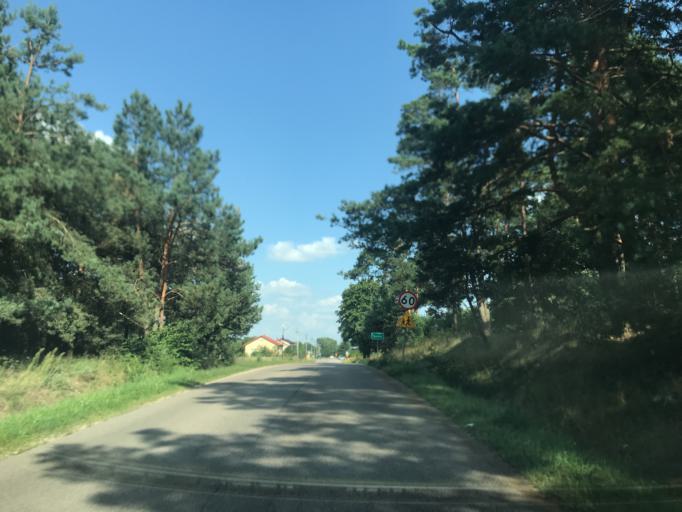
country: PL
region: Masovian Voivodeship
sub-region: Powiat mlawski
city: Wisniewo
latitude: 53.1118
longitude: 20.3272
